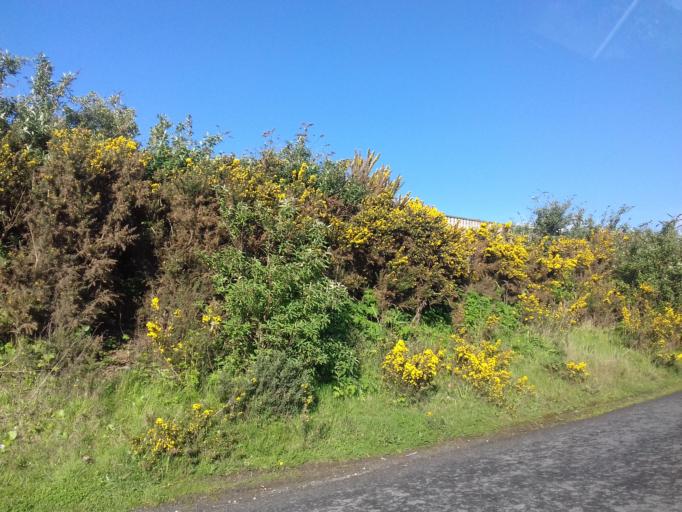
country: IE
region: Leinster
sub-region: Wicklow
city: Kilpedder
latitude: 53.1168
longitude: -6.0993
